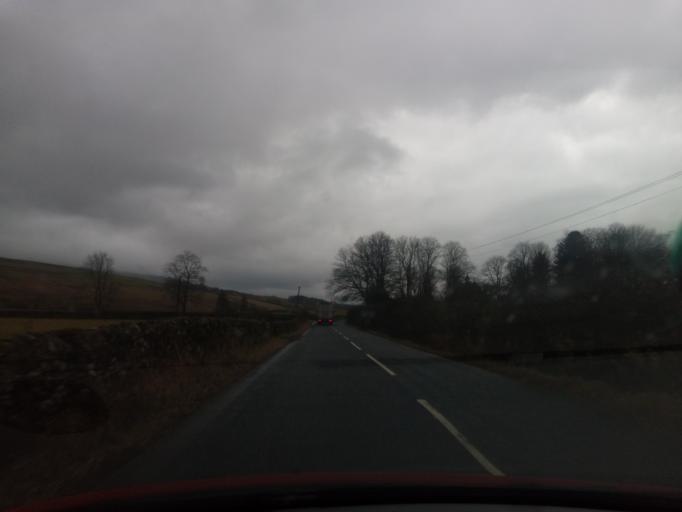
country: GB
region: Scotland
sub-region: The Scottish Borders
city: Hawick
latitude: 55.2647
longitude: -2.6905
